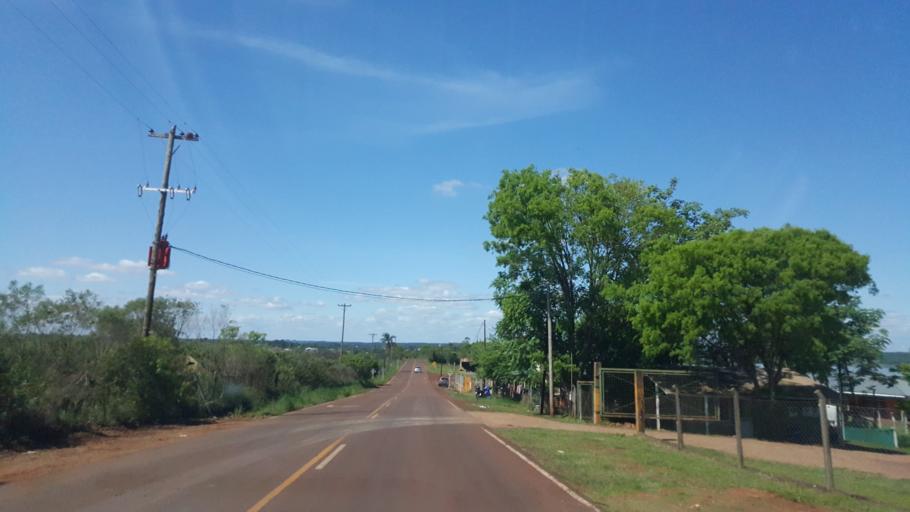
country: AR
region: Misiones
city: Garupa
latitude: -27.4991
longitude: -55.8454
